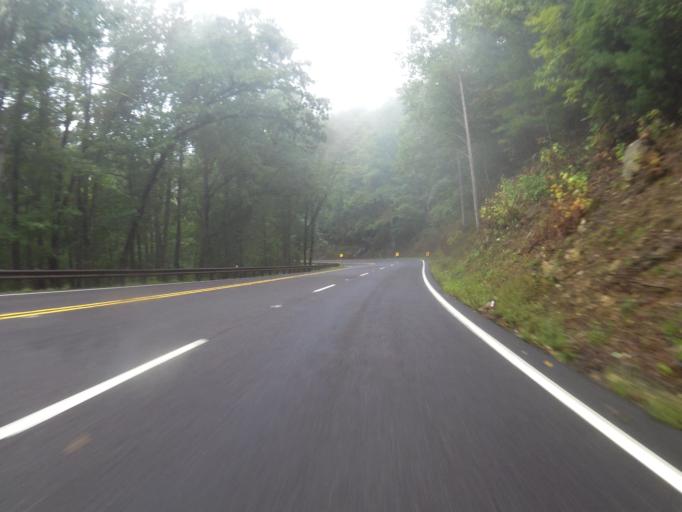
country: US
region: Virginia
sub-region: Rappahannock County
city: Washington
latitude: 38.6639
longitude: -78.2951
